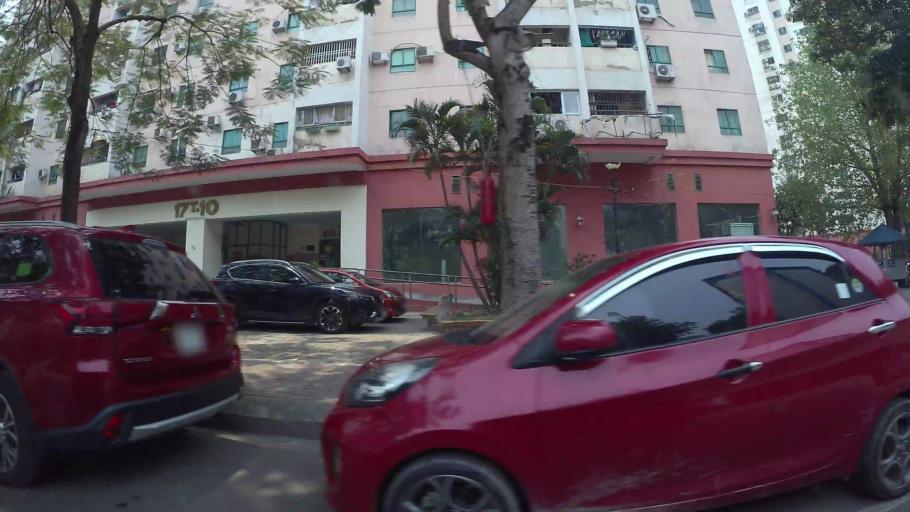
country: VN
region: Ha Noi
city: Thanh Xuan
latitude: 21.0109
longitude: 105.8045
